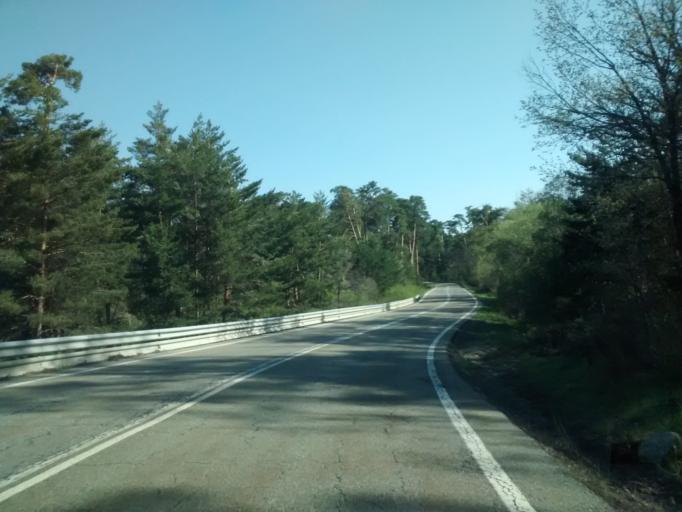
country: ES
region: Castille and Leon
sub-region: Provincia de Segovia
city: San Ildefonso
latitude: 40.8567
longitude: -4.0267
